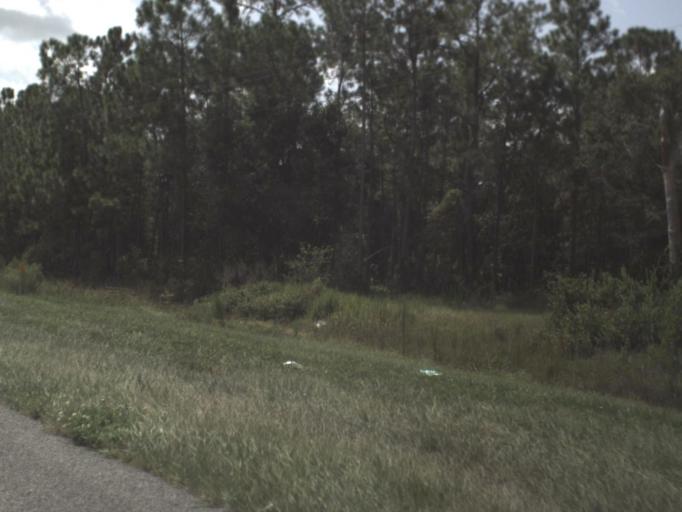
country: US
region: Florida
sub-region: Polk County
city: Crooked Lake Park
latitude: 27.7676
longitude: -81.5962
